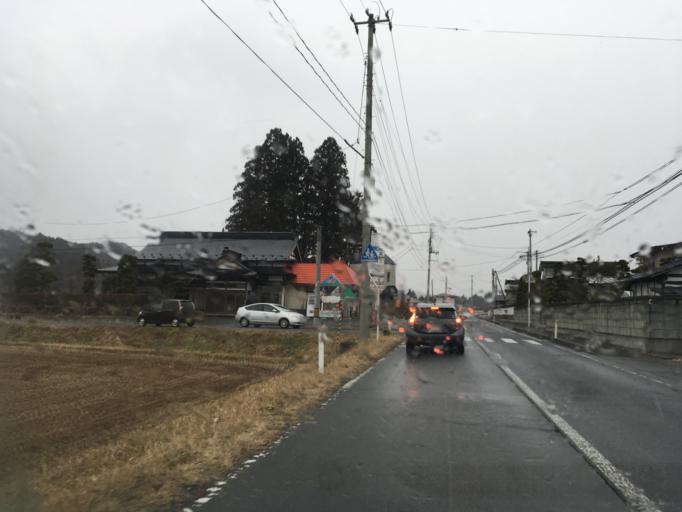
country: JP
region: Iwate
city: Ichinoseki
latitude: 38.8521
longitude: 140.9562
